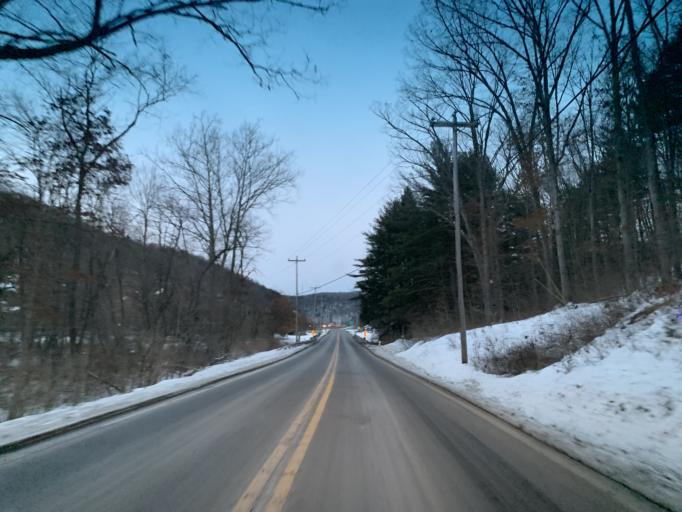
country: US
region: West Virginia
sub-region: Morgan County
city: Berkeley Springs
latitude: 39.6801
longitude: -78.4814
